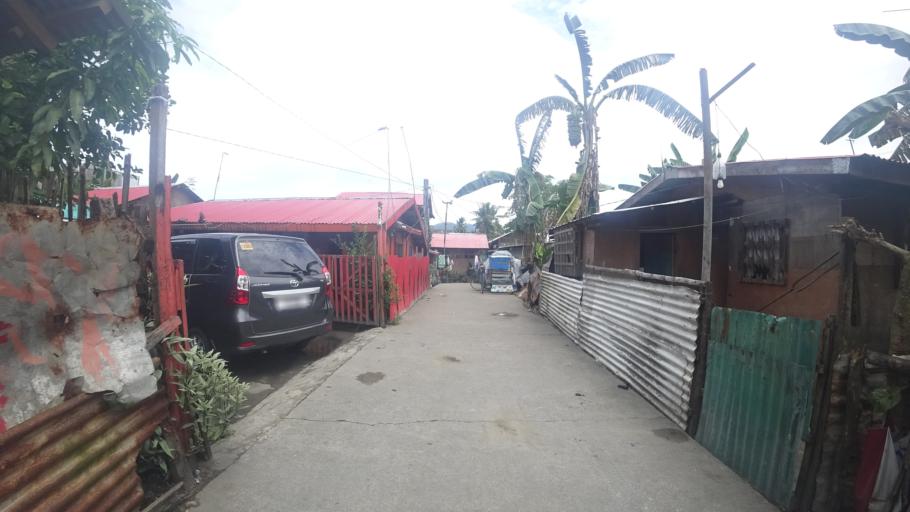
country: PH
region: Eastern Visayas
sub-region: Province of Leyte
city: Baras
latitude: 11.2052
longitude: 125.0112
